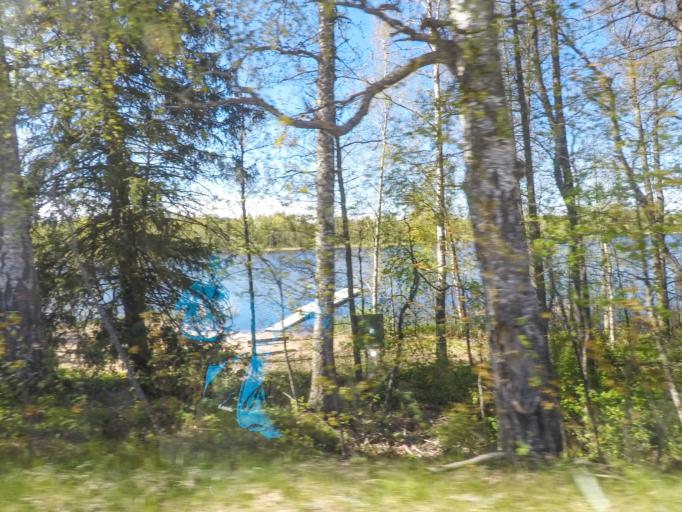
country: FI
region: Uusimaa
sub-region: Helsinki
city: Sammatti
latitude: 60.3412
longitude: 23.8014
